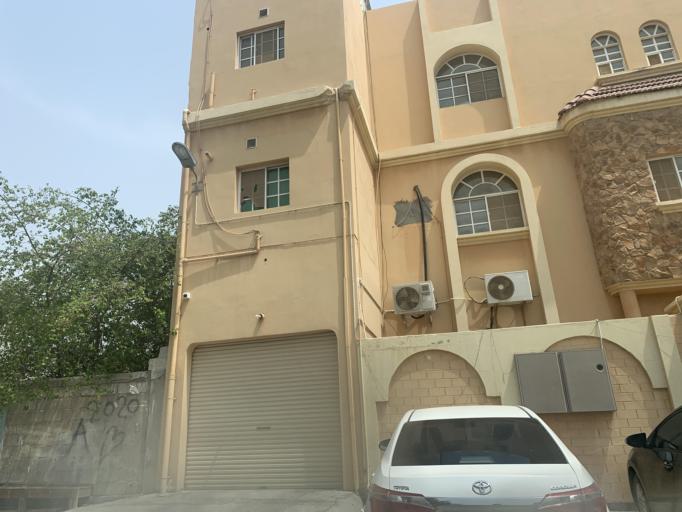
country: BH
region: Manama
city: Jidd Hafs
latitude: 26.1973
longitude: 50.4661
